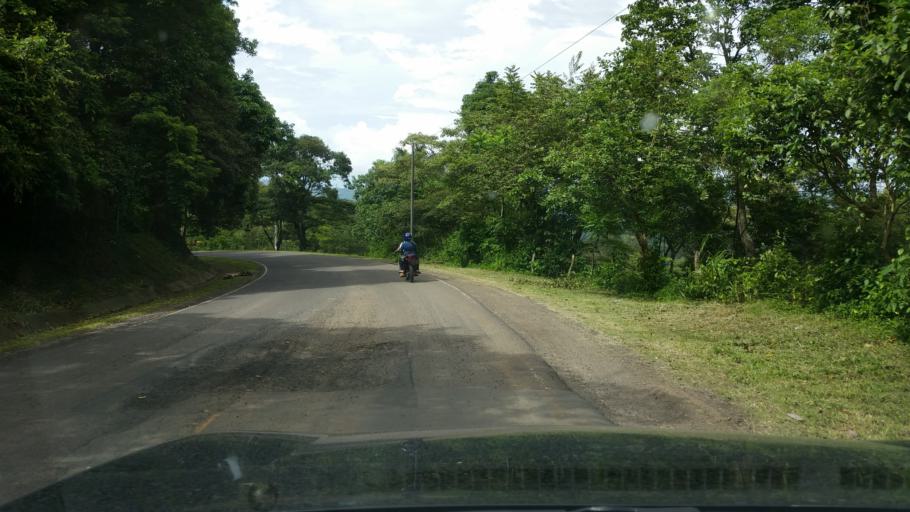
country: NI
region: Matagalpa
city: San Ramon
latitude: 12.9667
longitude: -85.8533
